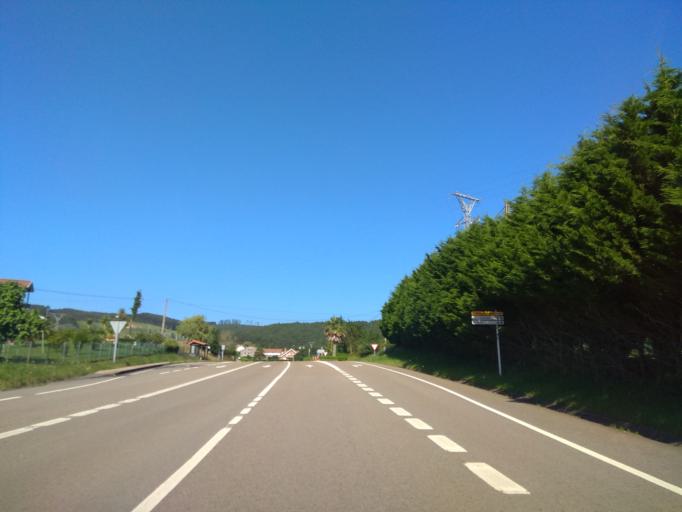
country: ES
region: Cantabria
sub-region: Provincia de Cantabria
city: Bareyo
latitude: 43.4676
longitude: -3.6640
